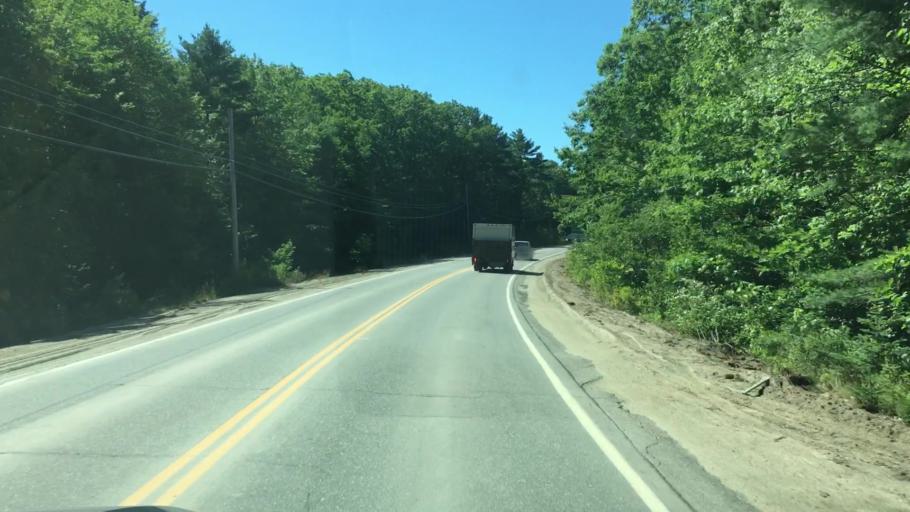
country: US
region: Maine
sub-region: Hancock County
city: Sedgwick
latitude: 44.3817
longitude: -68.5689
